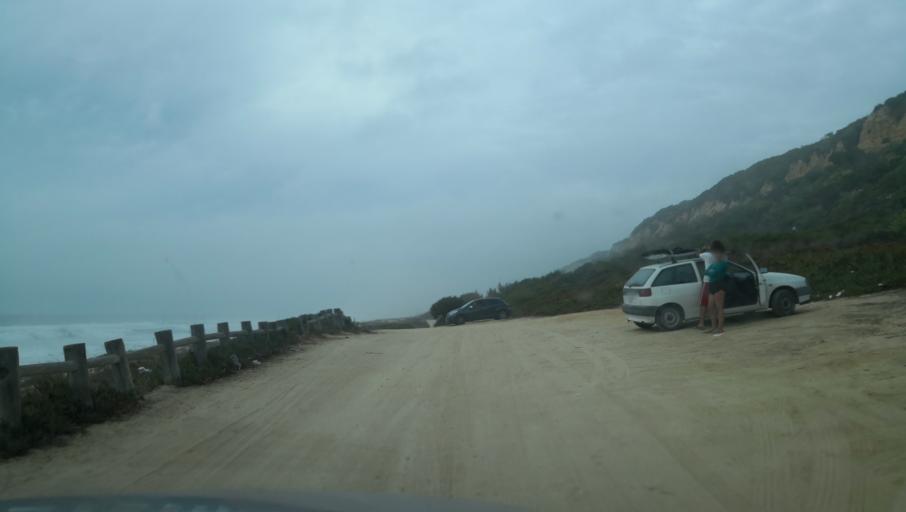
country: PT
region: Setubal
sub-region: Almada
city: Charneca
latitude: 38.5617
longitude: -9.1907
